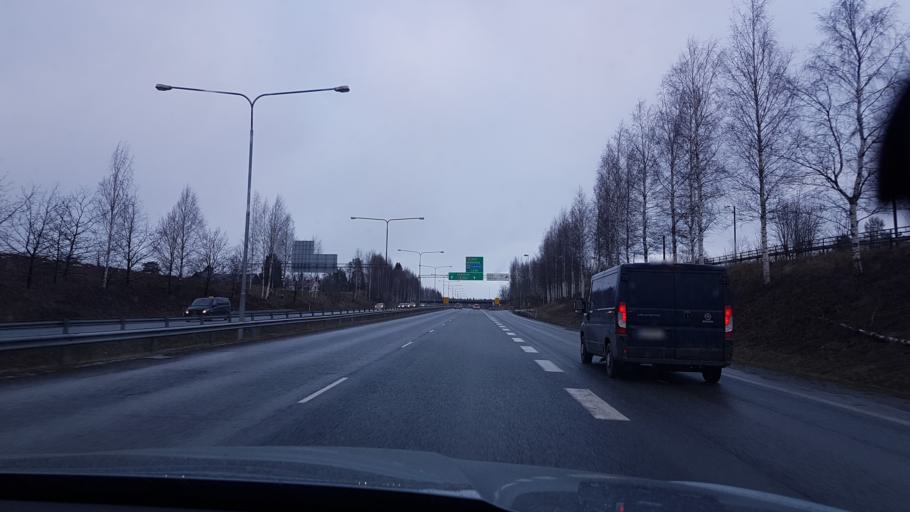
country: FI
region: Pirkanmaa
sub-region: Tampere
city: Tampere
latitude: 61.4836
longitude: 23.8736
